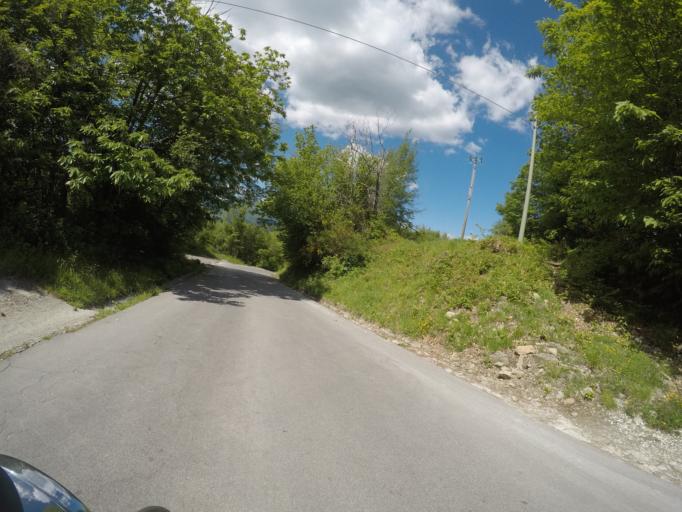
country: IT
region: Tuscany
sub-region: Provincia di Lucca
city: Minucciano
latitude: 44.1616
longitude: 10.2061
